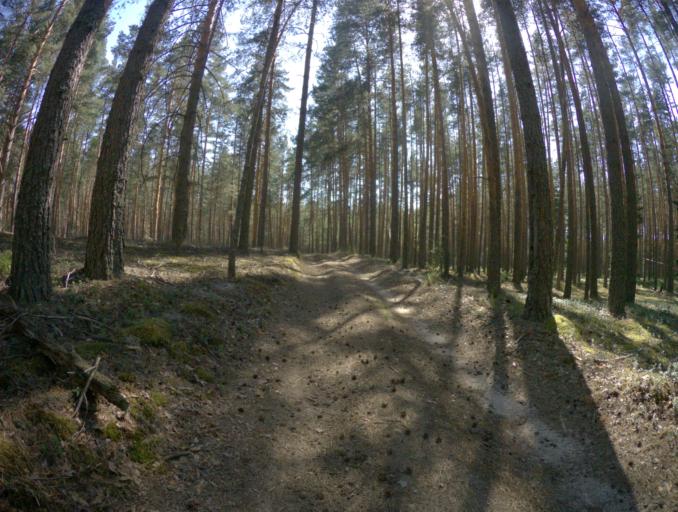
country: RU
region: Vladimir
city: Vyazniki
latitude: 56.3892
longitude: 42.2350
